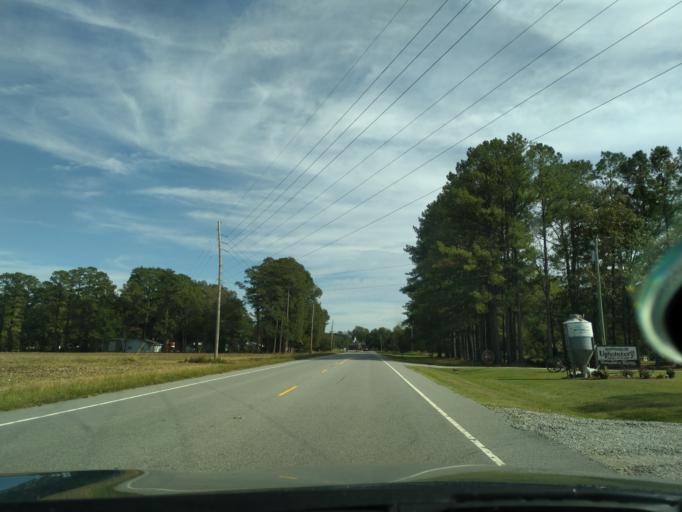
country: US
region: North Carolina
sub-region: Beaufort County
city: River Road
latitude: 35.5148
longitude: -76.9142
